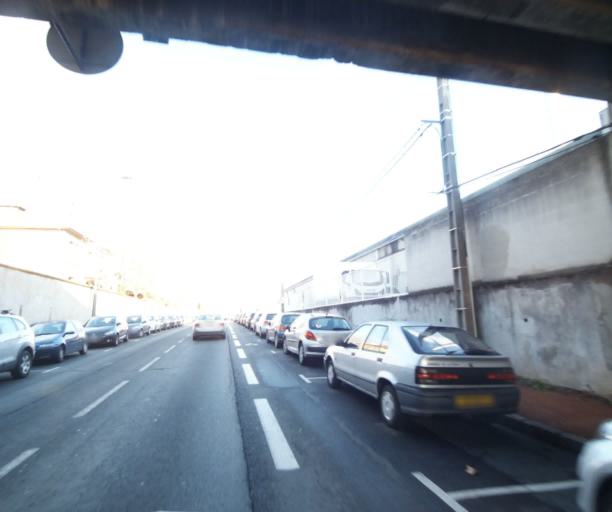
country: FR
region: Rhone-Alpes
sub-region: Departement de la Loire
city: Le Coteau
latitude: 46.0433
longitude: 4.0810
